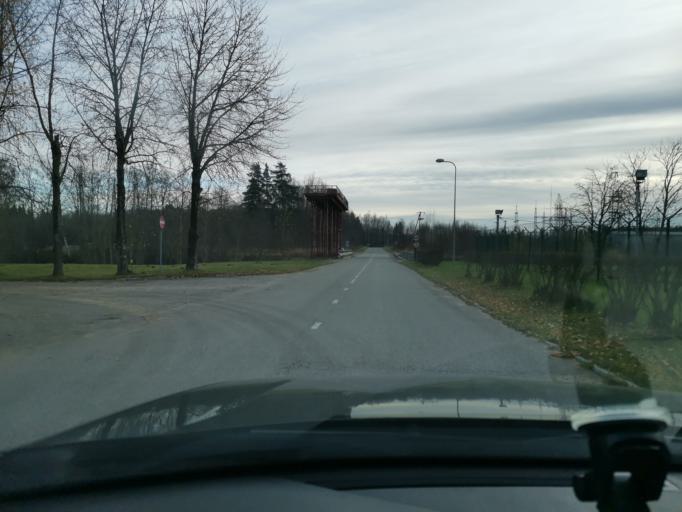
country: EE
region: Ida-Virumaa
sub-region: Sillamaee linn
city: Sillamae
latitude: 59.2733
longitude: 27.9115
